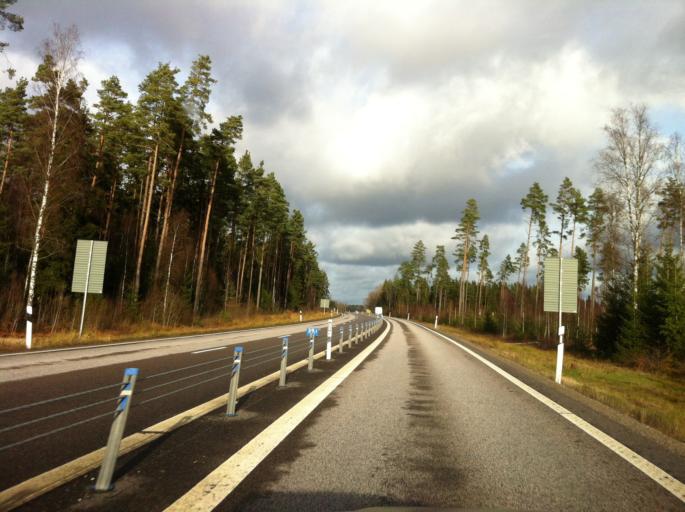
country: SE
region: Kronoberg
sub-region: Alvesta Kommun
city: Vislanda
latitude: 56.7100
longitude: 14.4275
